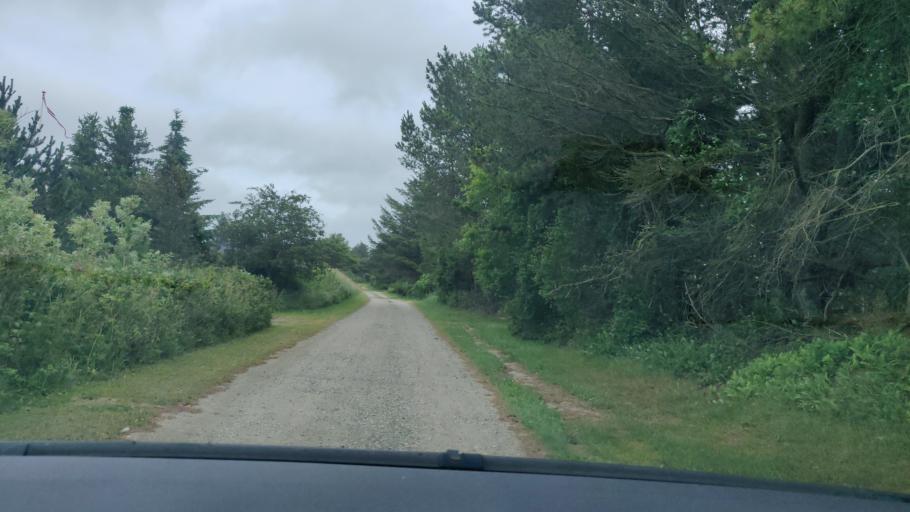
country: DK
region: North Denmark
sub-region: Jammerbugt Kommune
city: Pandrup
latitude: 57.2573
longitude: 9.6015
